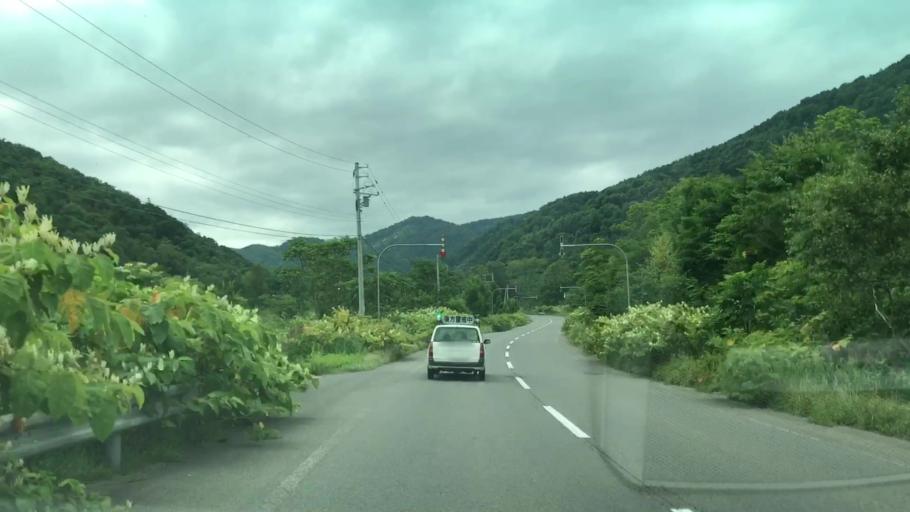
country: JP
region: Hokkaido
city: Yoichi
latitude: 43.0258
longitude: 140.8665
